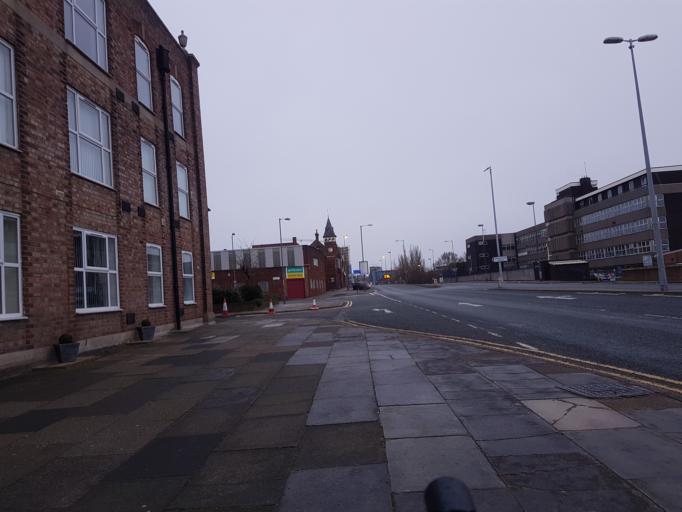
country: GB
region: England
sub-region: Liverpool
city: Liverpool
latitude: 53.4151
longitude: -2.9786
